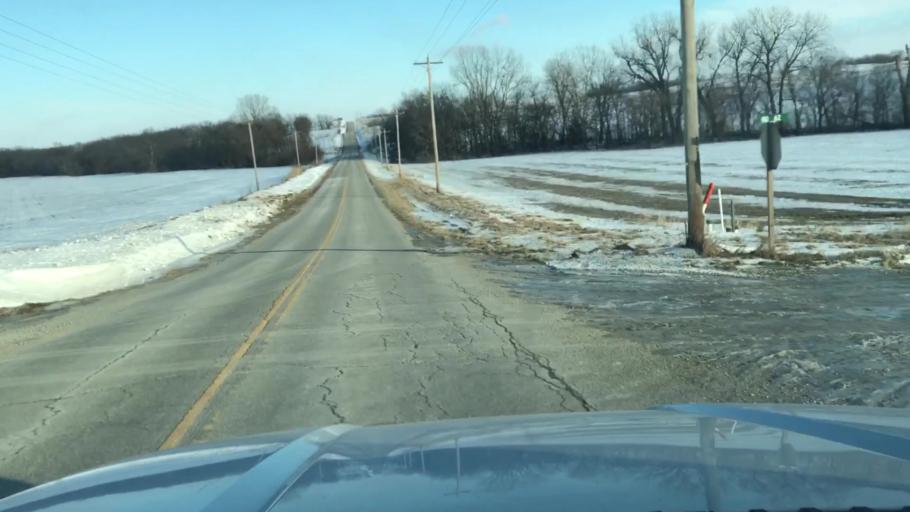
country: US
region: Missouri
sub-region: Andrew County
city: Savannah
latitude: 40.0246
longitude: -94.9075
